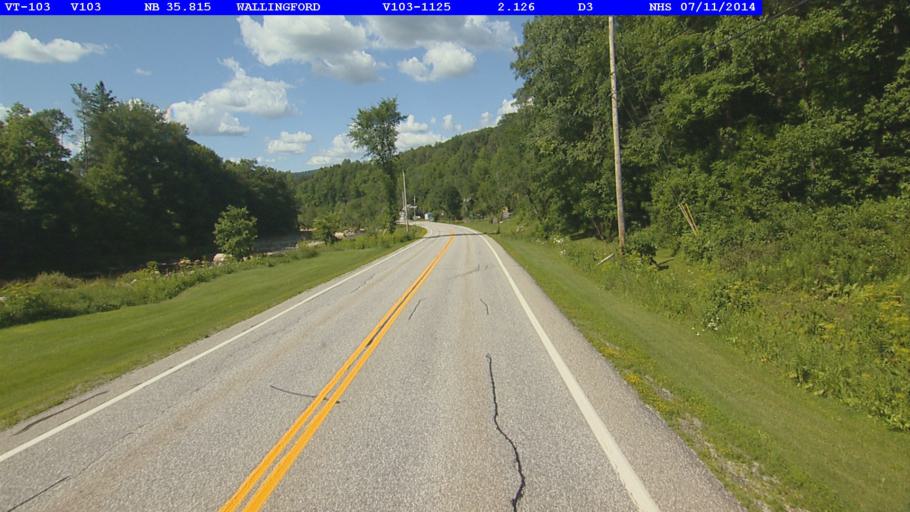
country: US
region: Vermont
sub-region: Rutland County
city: Rutland
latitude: 43.4800
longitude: -72.8776
